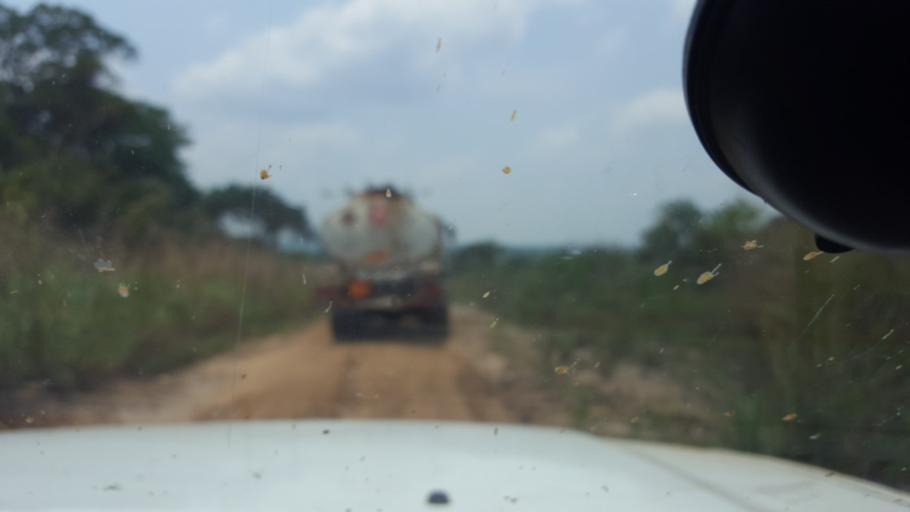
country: CD
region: Bandundu
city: Mushie
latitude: -3.7515
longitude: 16.6403
